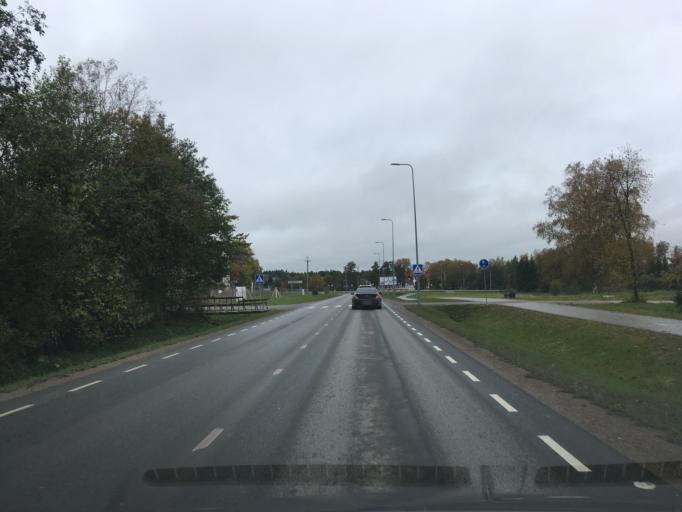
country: EE
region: Harju
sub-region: Saku vald
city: Saku
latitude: 59.2983
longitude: 24.6526
